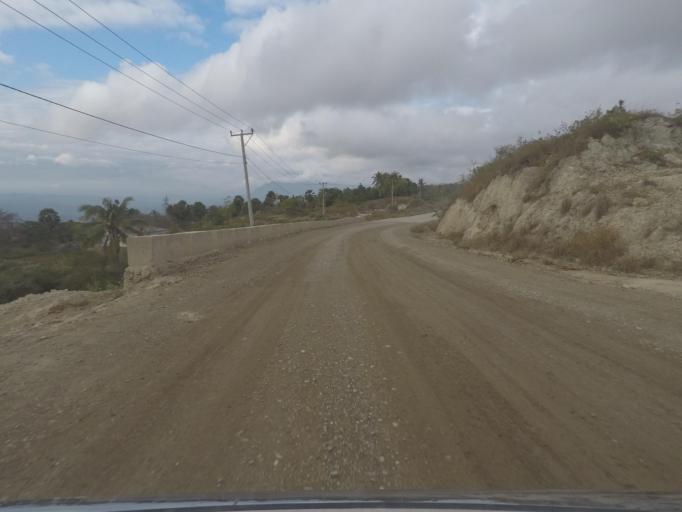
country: TL
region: Baucau
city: Baucau
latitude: -8.5053
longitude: 126.4451
